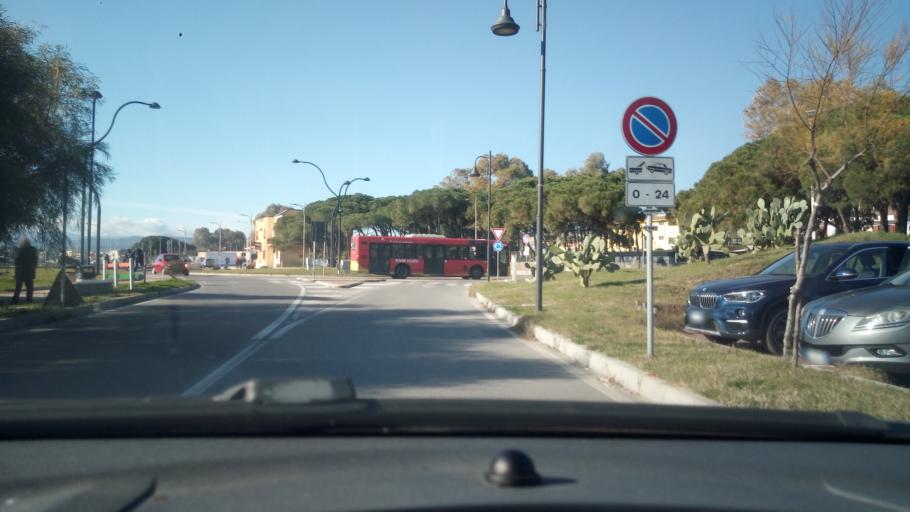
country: IT
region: Calabria
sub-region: Provincia di Catanzaro
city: Barone
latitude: 38.8283
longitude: 16.6373
